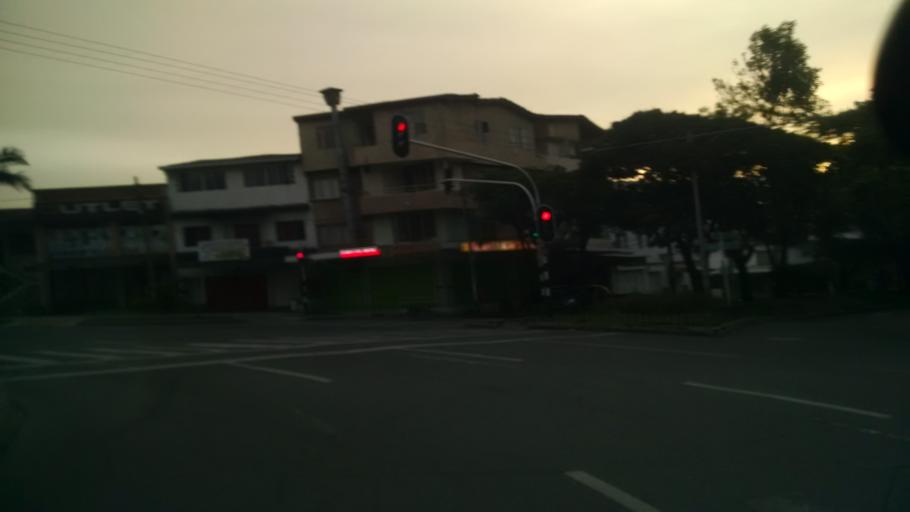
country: CO
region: Antioquia
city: Medellin
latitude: 6.2431
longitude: -75.6027
